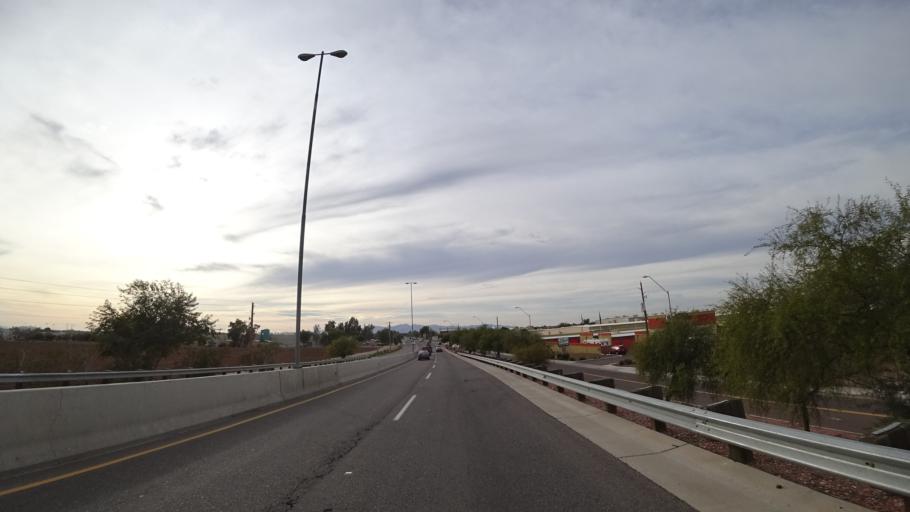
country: US
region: Arizona
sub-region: Maricopa County
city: Peoria
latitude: 33.5667
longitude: -112.2223
